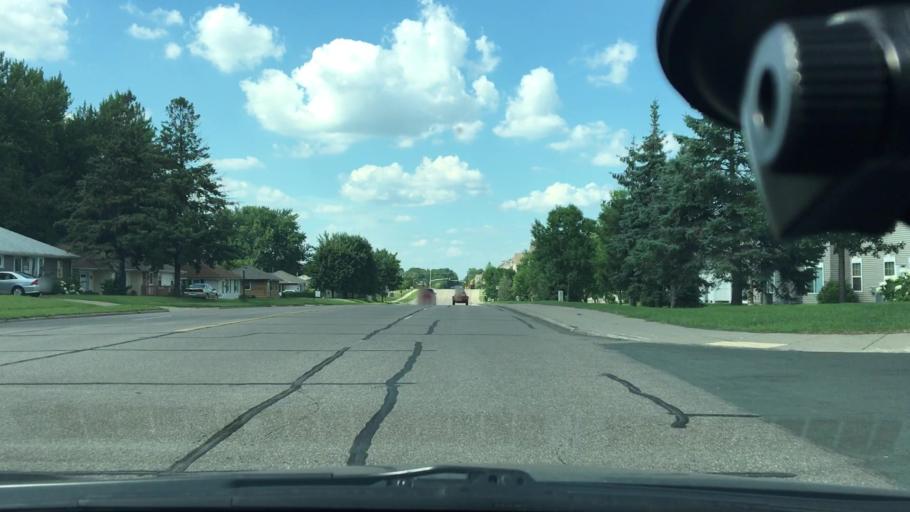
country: US
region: Minnesota
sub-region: Hennepin County
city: New Hope
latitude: 45.0510
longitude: -93.3804
